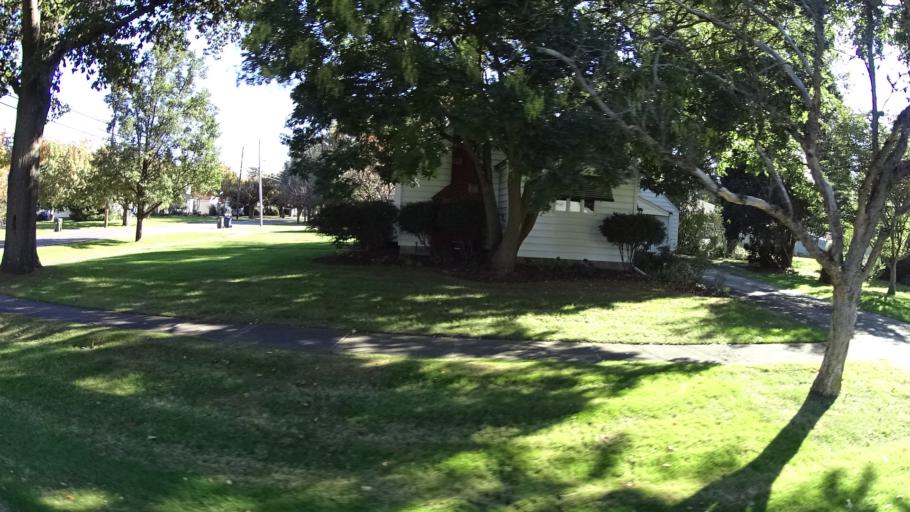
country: US
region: Ohio
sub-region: Lorain County
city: South Amherst
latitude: 41.3576
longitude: -82.2357
